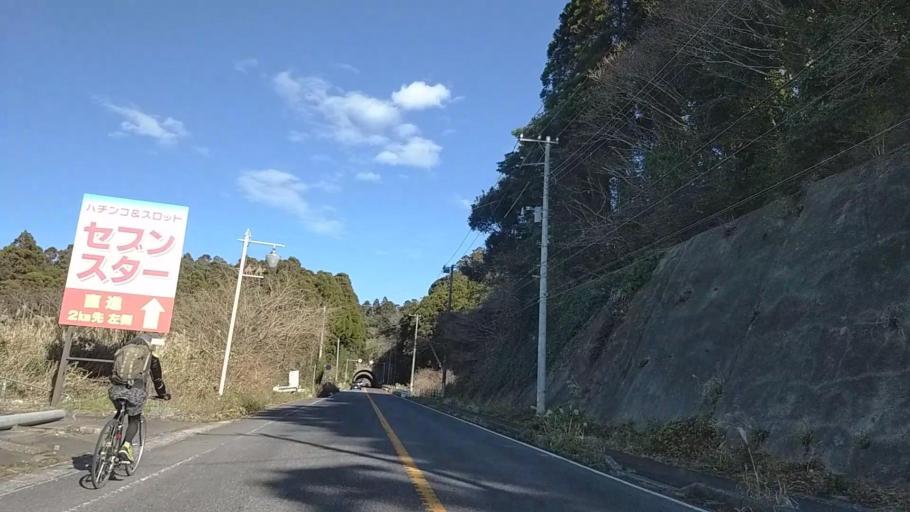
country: JP
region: Chiba
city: Ohara
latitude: 35.1950
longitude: 140.3649
